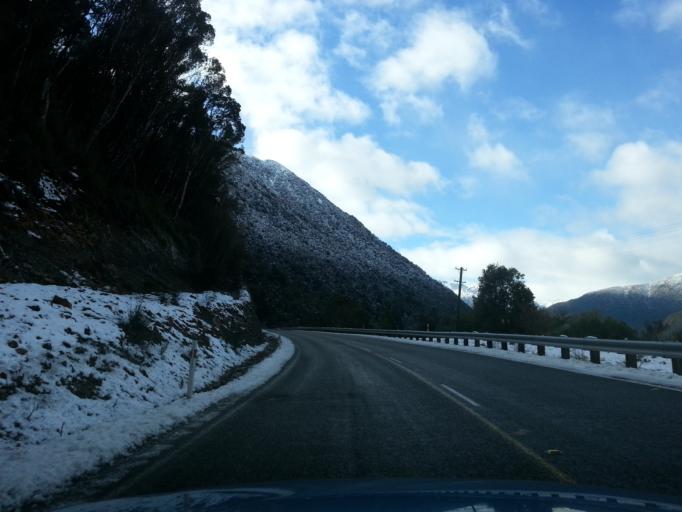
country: NZ
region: West Coast
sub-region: Grey District
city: Greymouth
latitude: -42.8019
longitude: 171.5762
